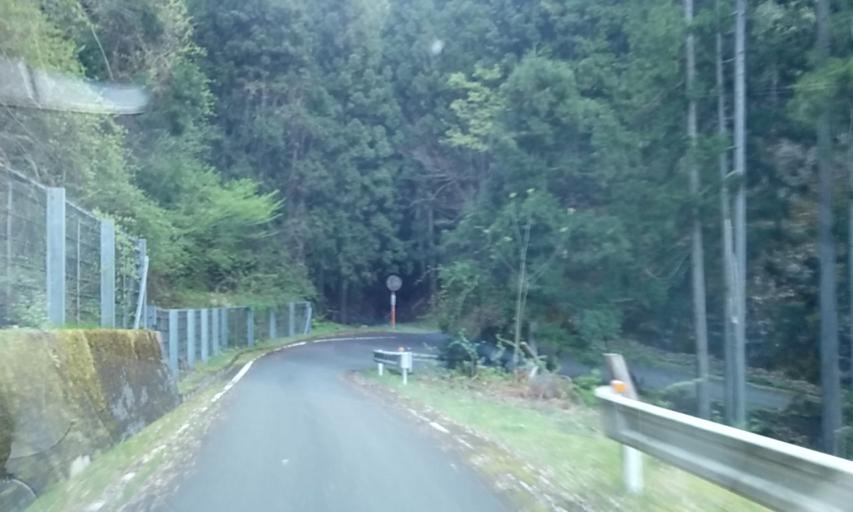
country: JP
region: Kyoto
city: Ayabe
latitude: 35.2569
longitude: 135.3291
